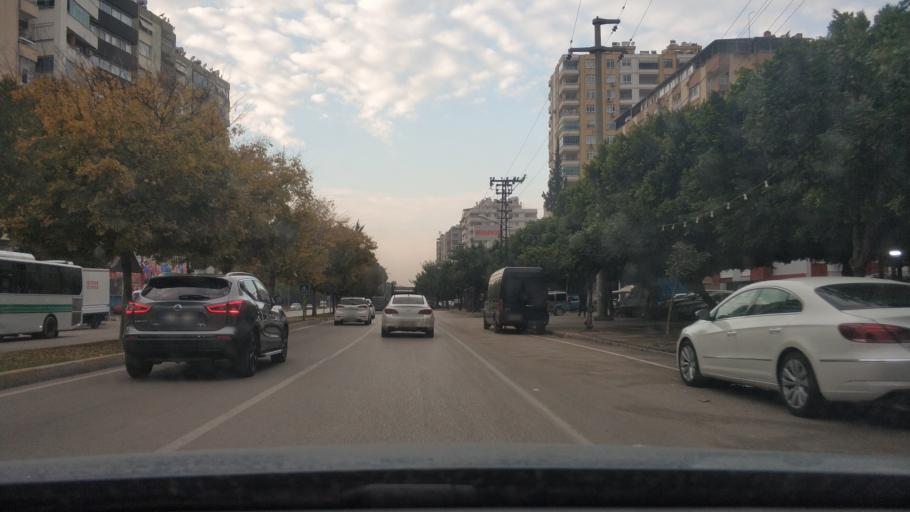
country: TR
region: Adana
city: Adana
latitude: 36.9984
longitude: 35.3177
